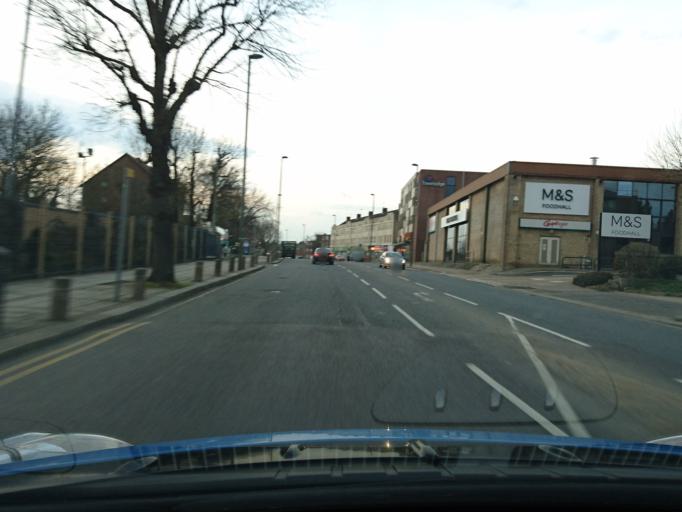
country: GB
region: England
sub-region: Greater London
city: Barnet
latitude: 51.6342
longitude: -0.1760
